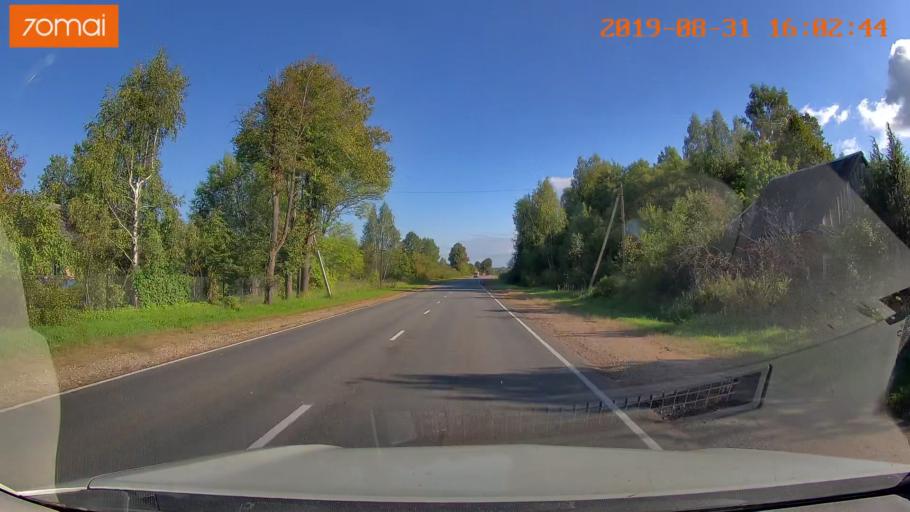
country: RU
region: Kaluga
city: Yukhnov
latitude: 54.6718
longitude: 35.3064
